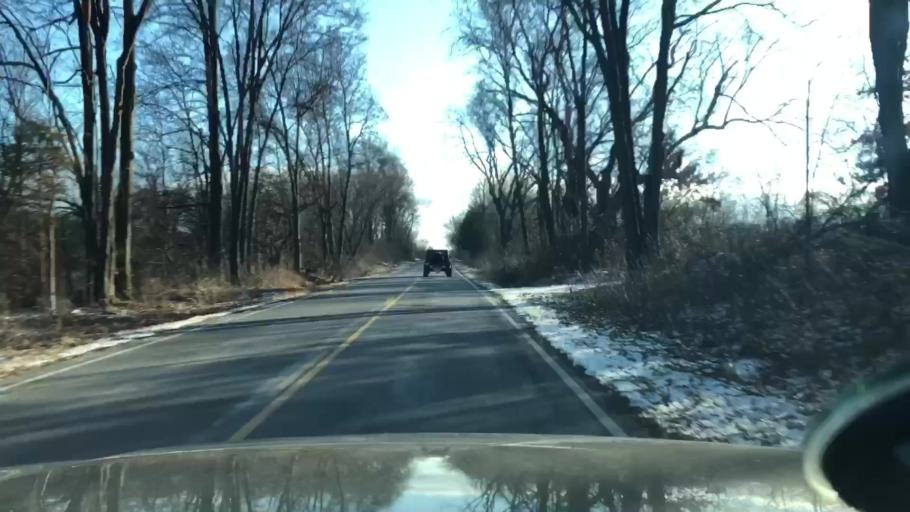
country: US
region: Michigan
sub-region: Jackson County
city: Vandercook Lake
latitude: 42.1286
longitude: -84.4515
